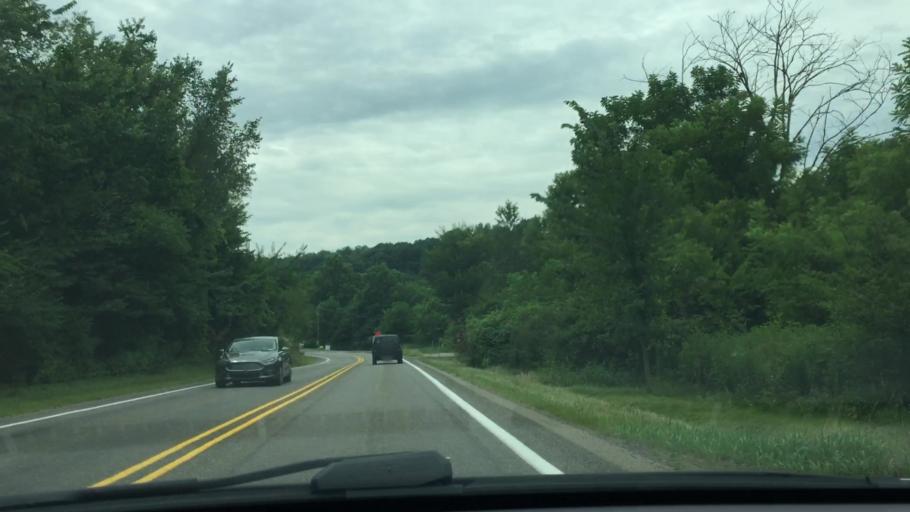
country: US
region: Pennsylvania
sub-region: Allegheny County
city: Oakdale
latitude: 40.4111
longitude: -80.1917
